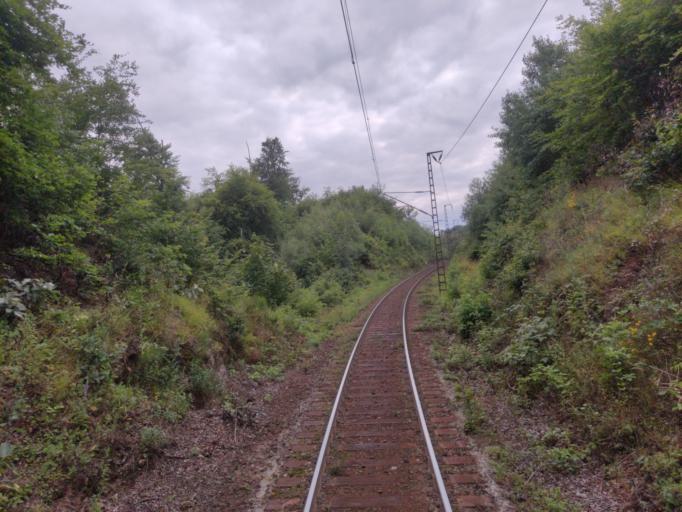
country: DE
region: Saxony-Anhalt
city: Blankenburg
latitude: 51.7913
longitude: 10.9263
